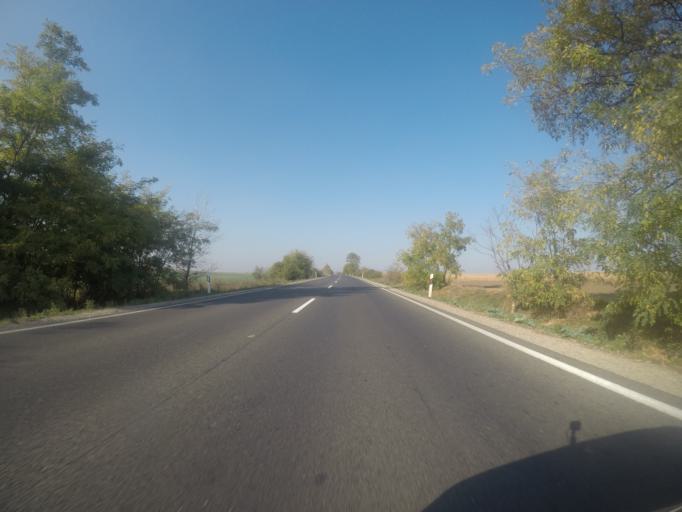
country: HU
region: Fejer
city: Racalmas
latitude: 47.0059
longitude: 18.9306
